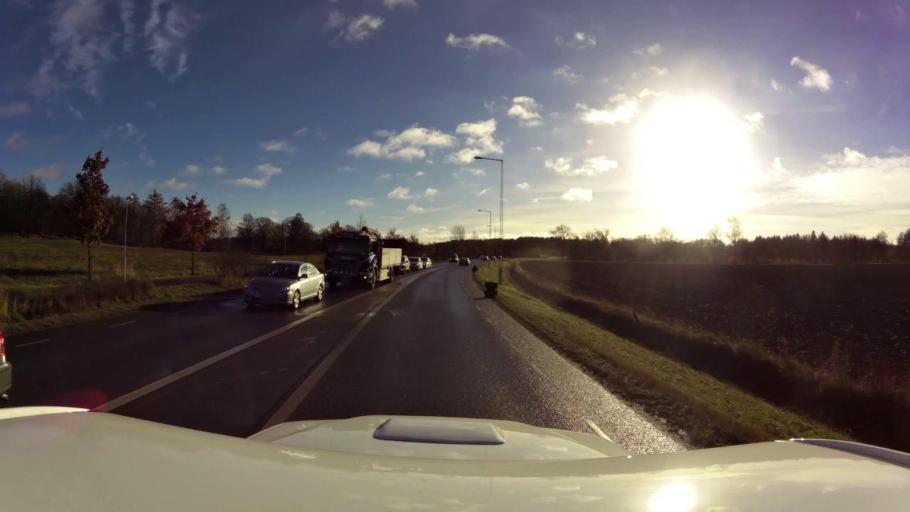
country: SE
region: OEstergoetland
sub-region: Linkopings Kommun
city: Linkoping
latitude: 58.3892
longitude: 15.6261
